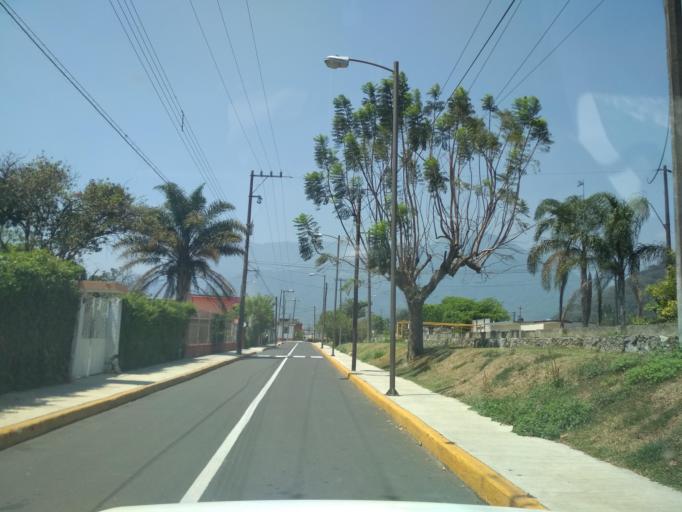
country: MX
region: Veracruz
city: Orizaba
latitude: 18.8360
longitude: -97.1106
